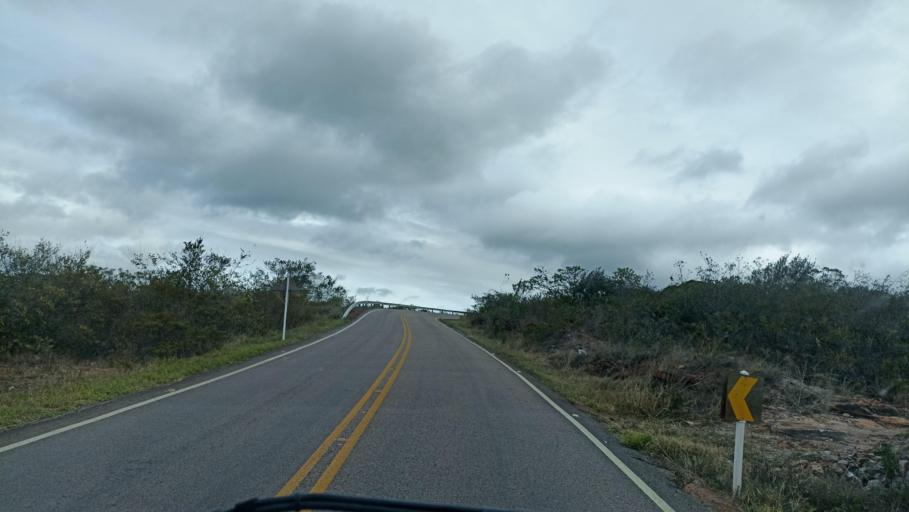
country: BR
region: Bahia
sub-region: Andarai
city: Vera Cruz
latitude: -12.9923
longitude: -41.3510
